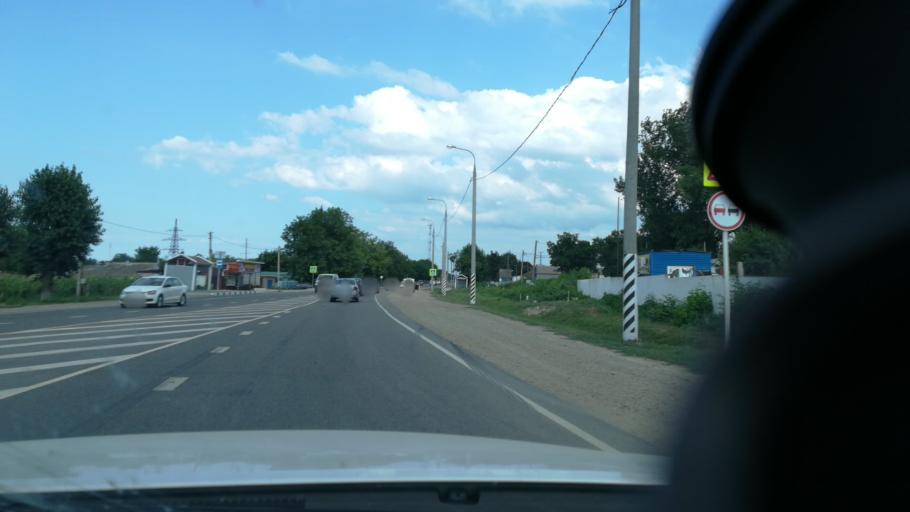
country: RU
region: Krasnodarskiy
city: Dzhiginka
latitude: 45.1268
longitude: 37.3272
